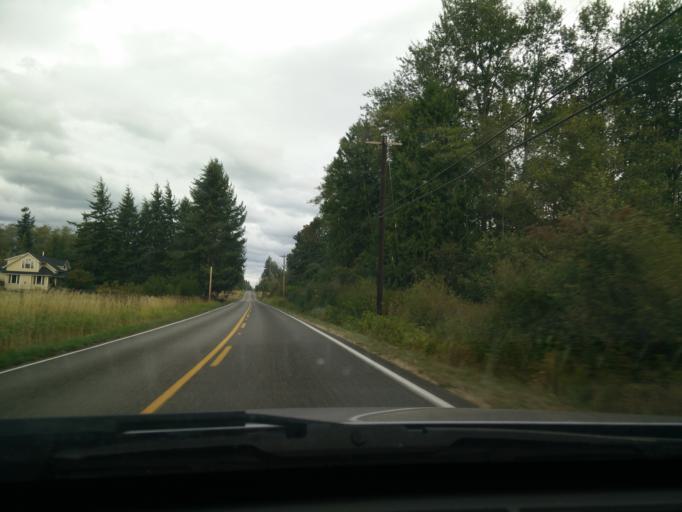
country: US
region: Washington
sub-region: Snohomish County
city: Stanwood
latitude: 48.2686
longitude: -122.3109
